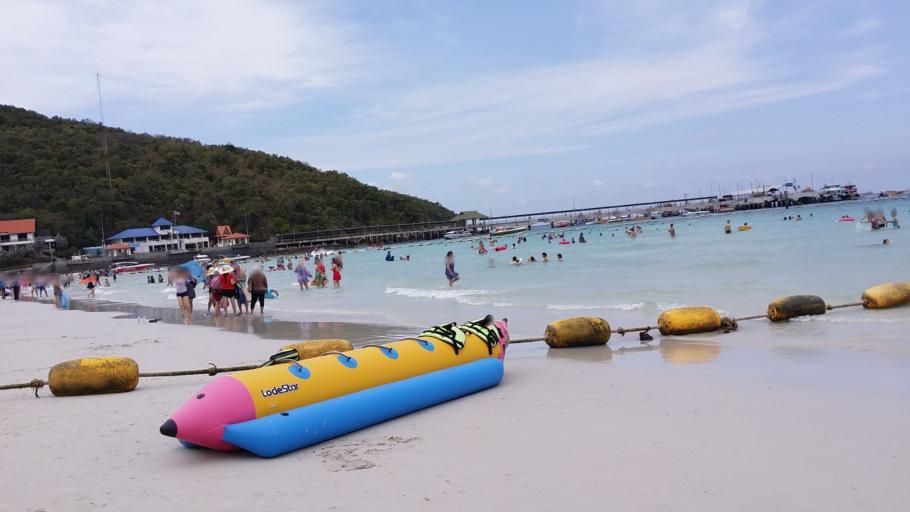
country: TH
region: Chon Buri
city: Ban Ko Lan
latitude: 12.9250
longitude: 100.7774
